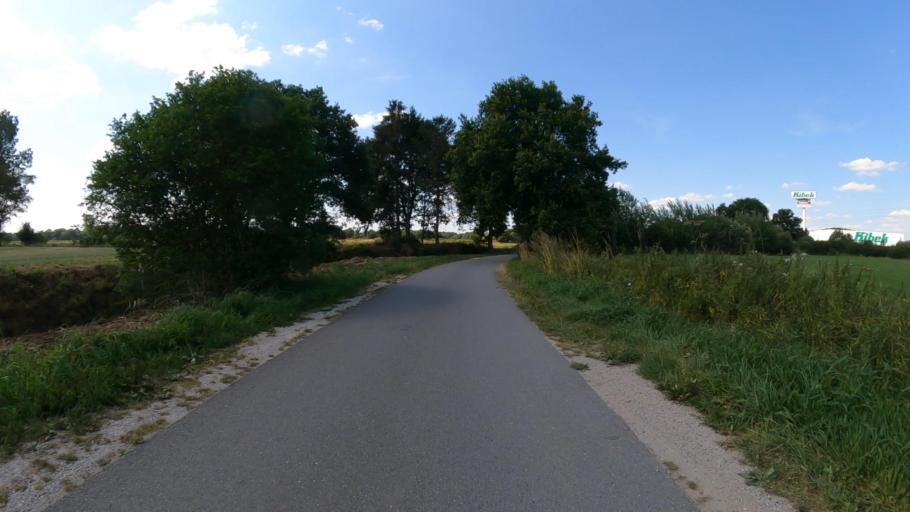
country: DE
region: Schleswig-Holstein
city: Seeth-Ekholt
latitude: 53.7380
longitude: 9.7159
